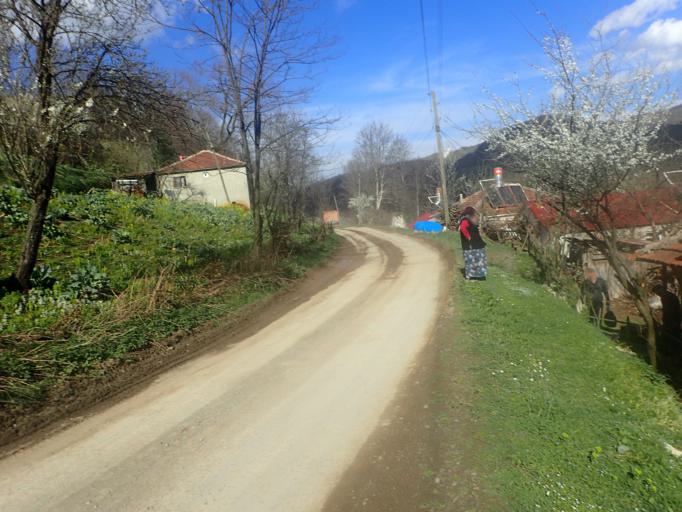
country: TR
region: Ordu
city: Kumru
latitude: 40.8033
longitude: 37.1929
